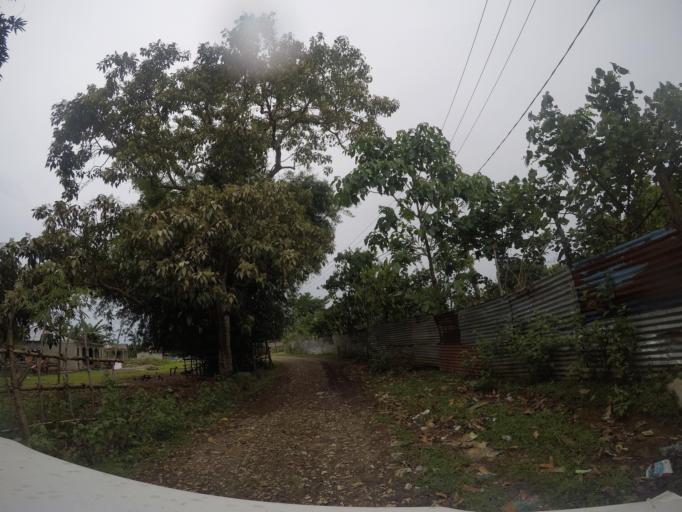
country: TL
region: Lautem
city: Lospalos
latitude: -8.5258
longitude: 127.0041
